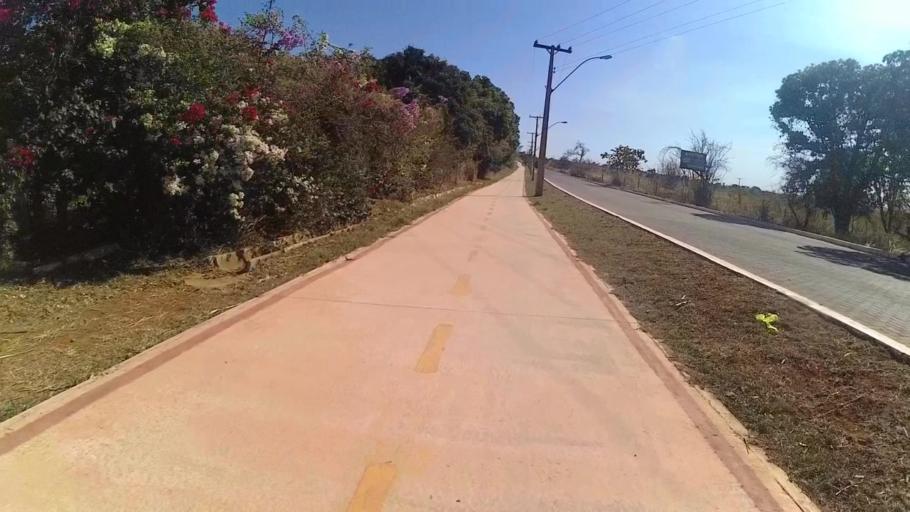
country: BR
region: Federal District
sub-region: Brasilia
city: Brasilia
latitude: -15.6571
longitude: -47.8977
